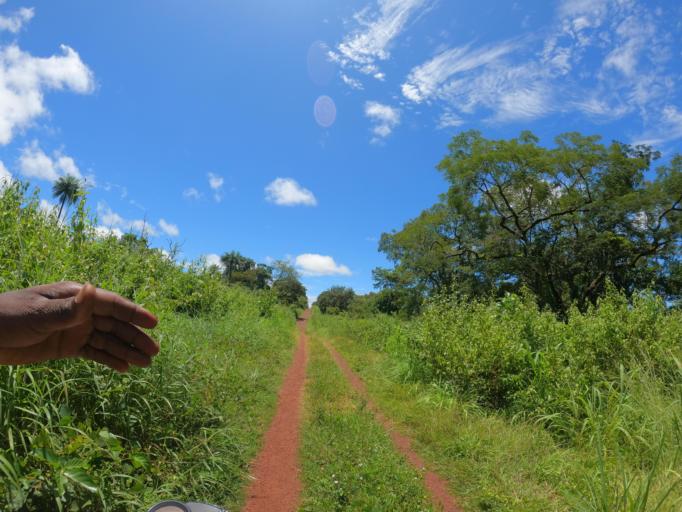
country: SL
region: Northern Province
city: Makeni
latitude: 9.0734
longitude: -12.2740
